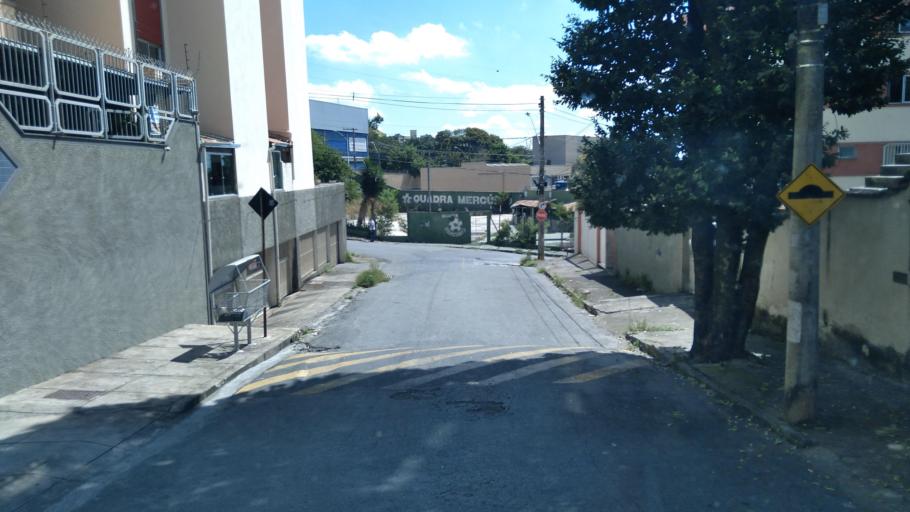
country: BR
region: Minas Gerais
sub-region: Belo Horizonte
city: Belo Horizonte
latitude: -19.8774
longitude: -43.9084
